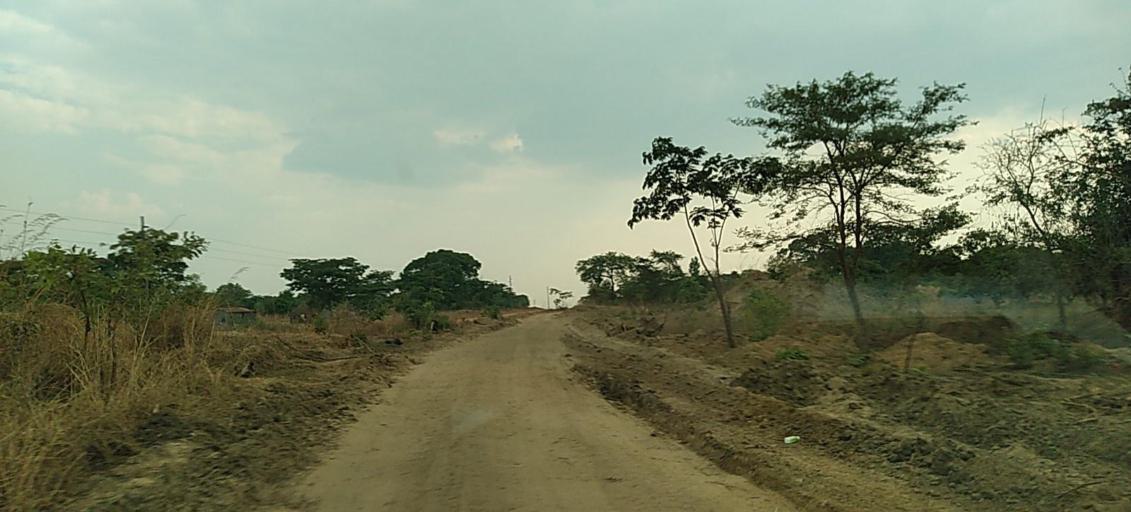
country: ZM
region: Copperbelt
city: Kalulushi
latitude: -12.9200
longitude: 27.9420
